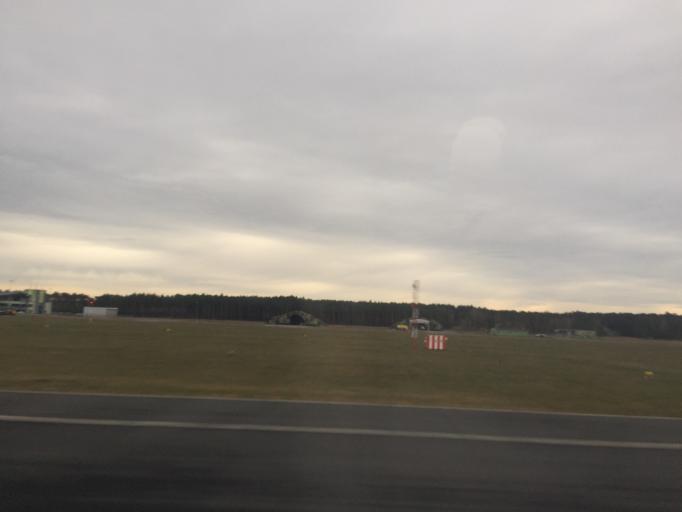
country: PL
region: Kujawsko-Pomorskie
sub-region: Bydgoszcz
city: Bydgoszcz
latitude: 53.0980
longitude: 17.9919
